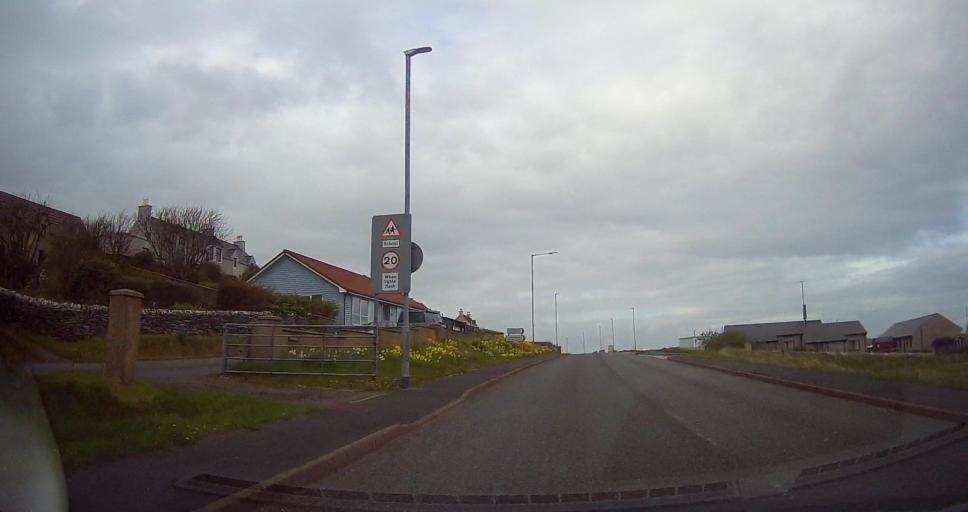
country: GB
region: Scotland
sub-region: Shetland Islands
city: Sandwick
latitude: 60.0441
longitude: -1.2289
